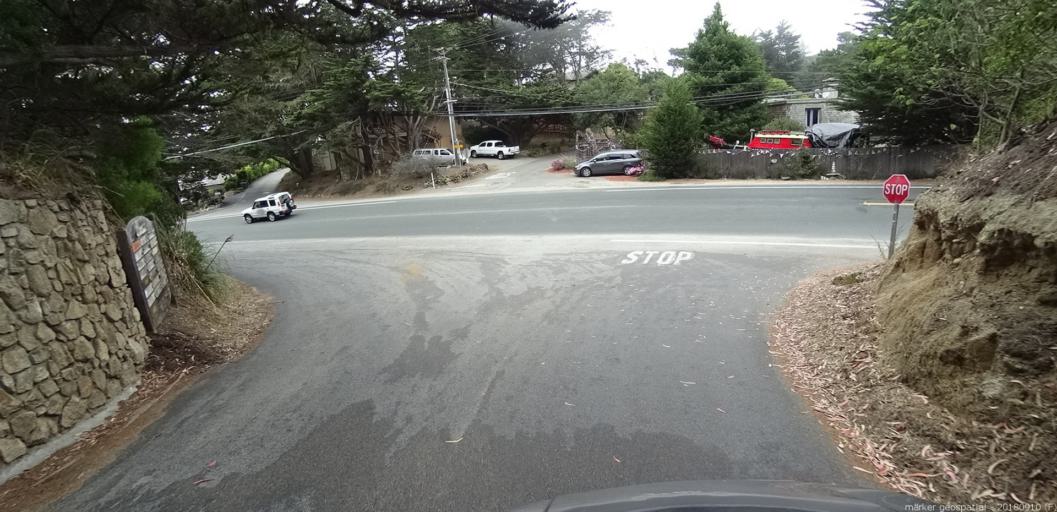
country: US
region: California
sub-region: Monterey County
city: Carmel-by-the-Sea
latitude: 36.4918
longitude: -121.9378
